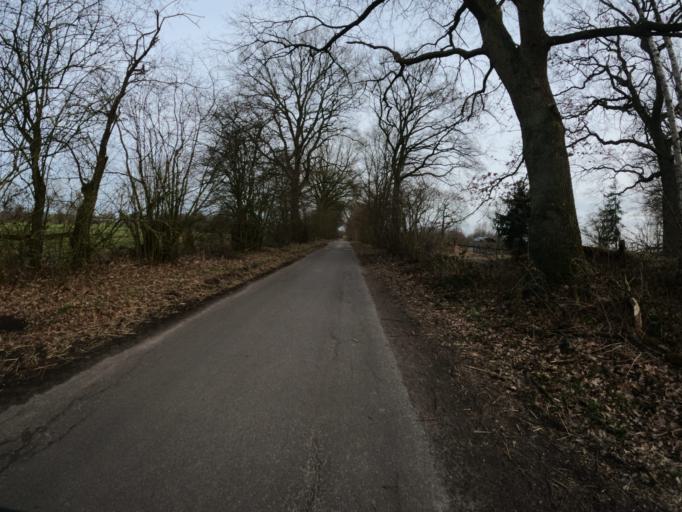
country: DE
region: Schleswig-Holstein
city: Rellingen
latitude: 53.5979
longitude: 9.7957
